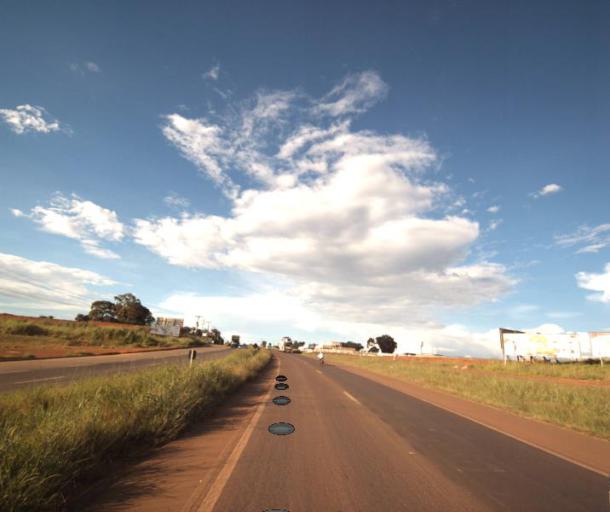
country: BR
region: Goias
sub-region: Anapolis
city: Anapolis
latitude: -16.3623
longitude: -48.9335
